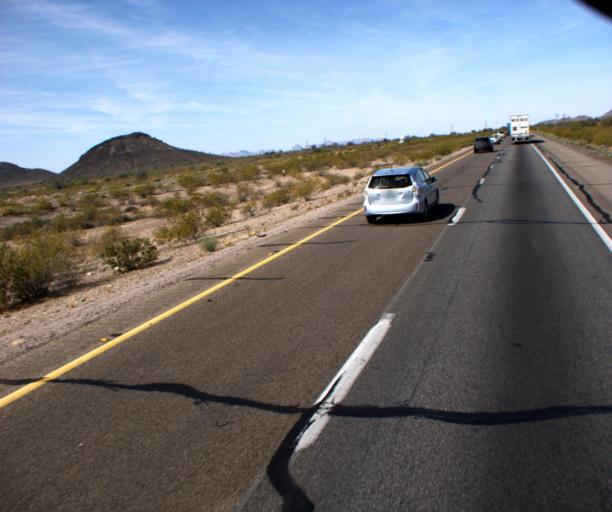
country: US
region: Arizona
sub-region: Maricopa County
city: Buckeye
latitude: 33.5097
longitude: -113.0037
